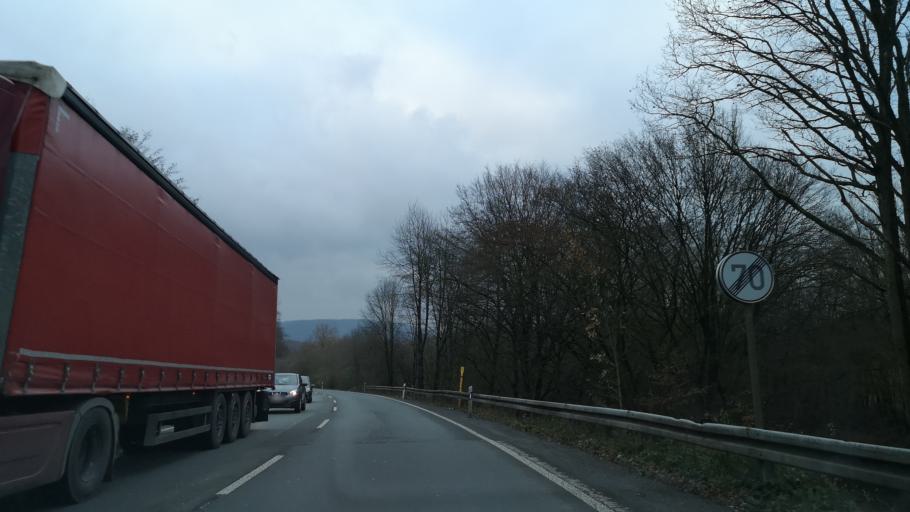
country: DE
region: North Rhine-Westphalia
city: Wetter (Ruhr)
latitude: 51.3541
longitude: 7.3921
